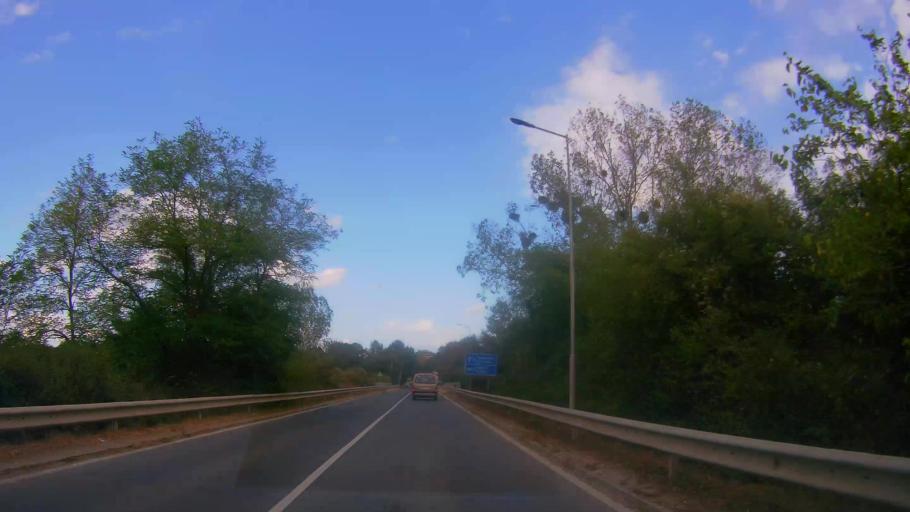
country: BG
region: Burgas
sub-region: Obshtina Primorsko
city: Primorsko
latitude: 42.2642
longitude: 27.7426
